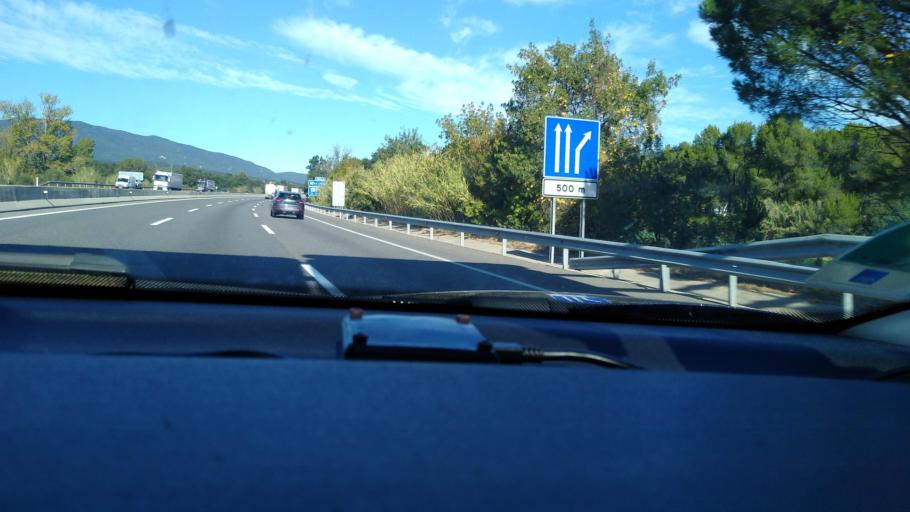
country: ES
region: Catalonia
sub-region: Provincia de Girona
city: la Jonquera
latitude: 42.3934
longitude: 2.8797
